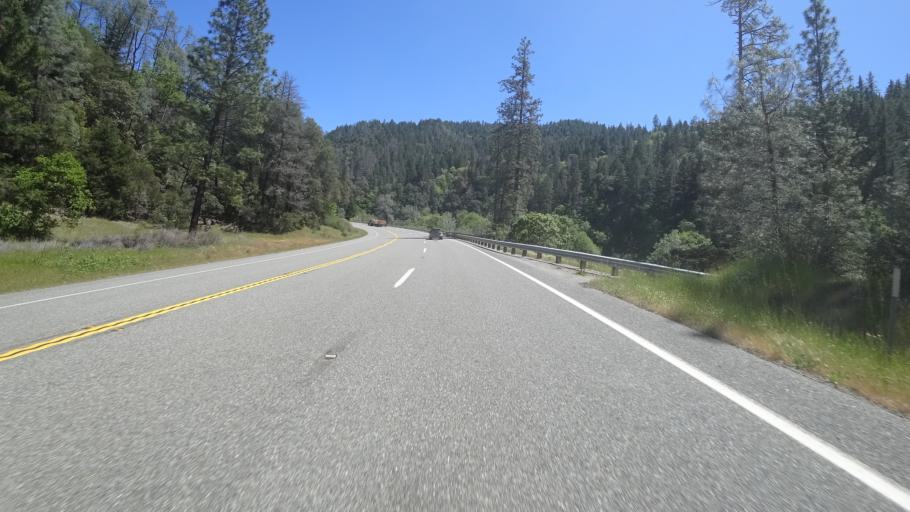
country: US
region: California
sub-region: Trinity County
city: Hayfork
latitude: 40.7361
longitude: -123.2333
